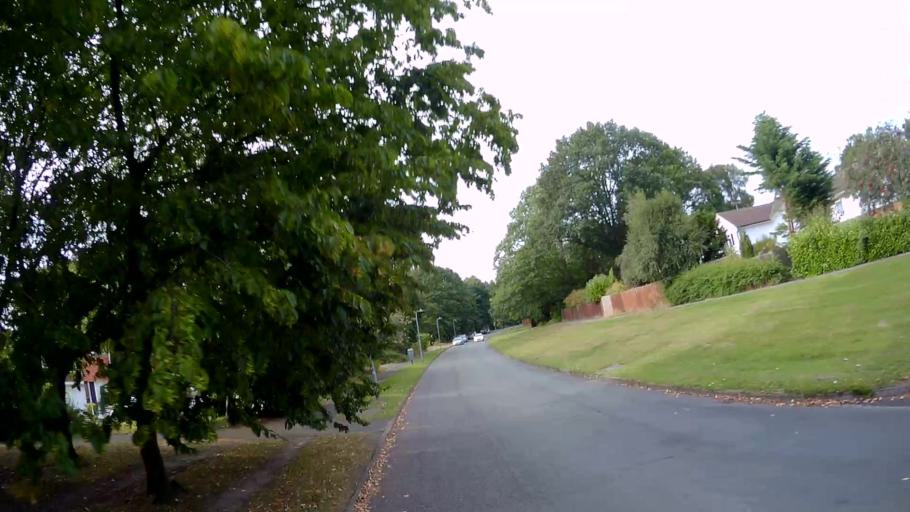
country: GB
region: England
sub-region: Bracknell Forest
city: Crowthorne
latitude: 51.3886
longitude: -0.7734
